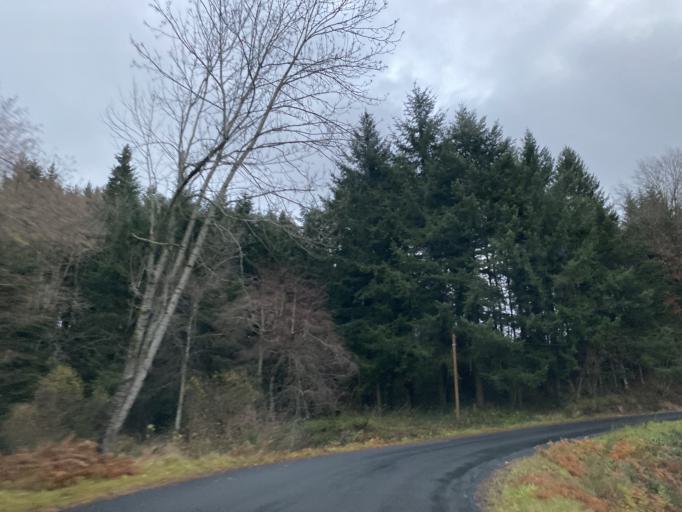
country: FR
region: Auvergne
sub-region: Departement du Puy-de-Dome
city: Cunlhat
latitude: 45.5705
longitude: 3.5610
